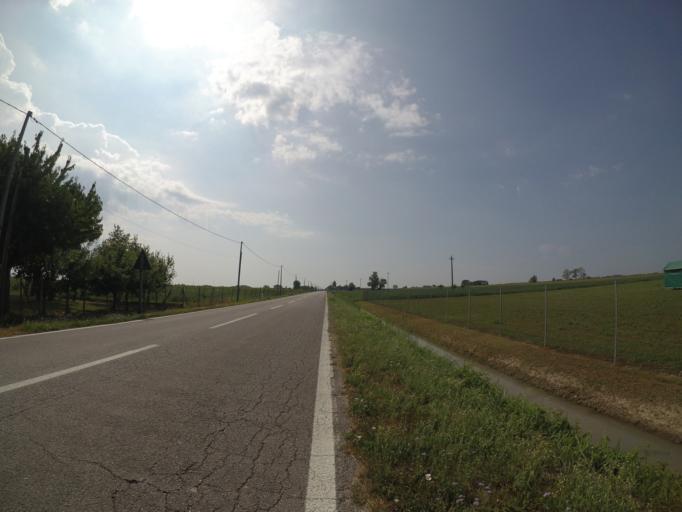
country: IT
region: Friuli Venezia Giulia
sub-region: Provincia di Udine
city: Pertegada
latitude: 45.7403
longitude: 13.0633
